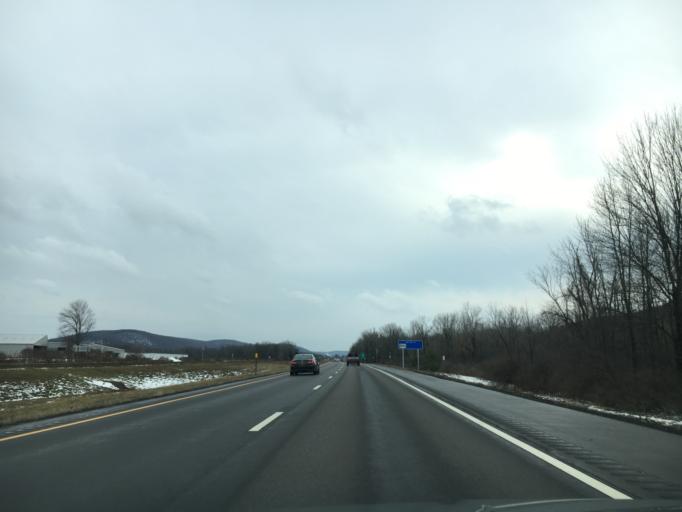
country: US
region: New York
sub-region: Cortland County
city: Homer
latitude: 42.7592
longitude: -76.1343
